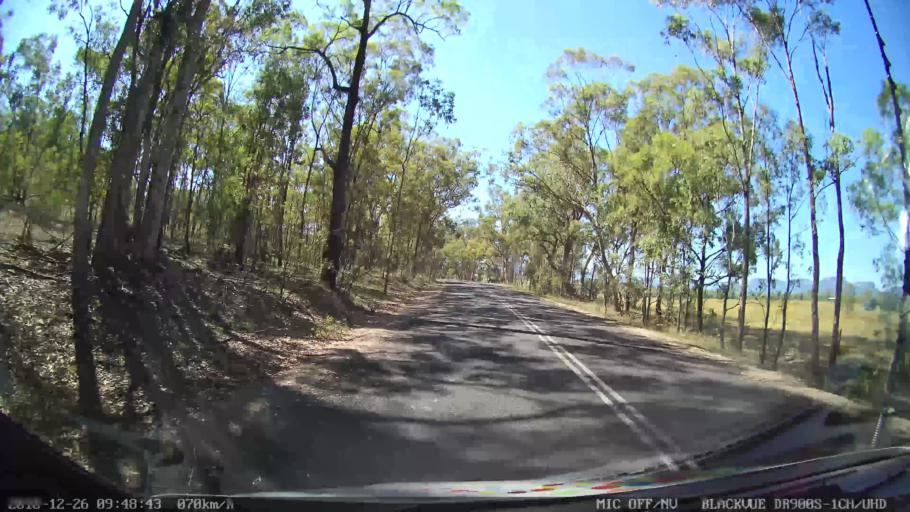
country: AU
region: New South Wales
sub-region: Mid-Western Regional
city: Kandos
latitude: -32.9892
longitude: 150.1169
